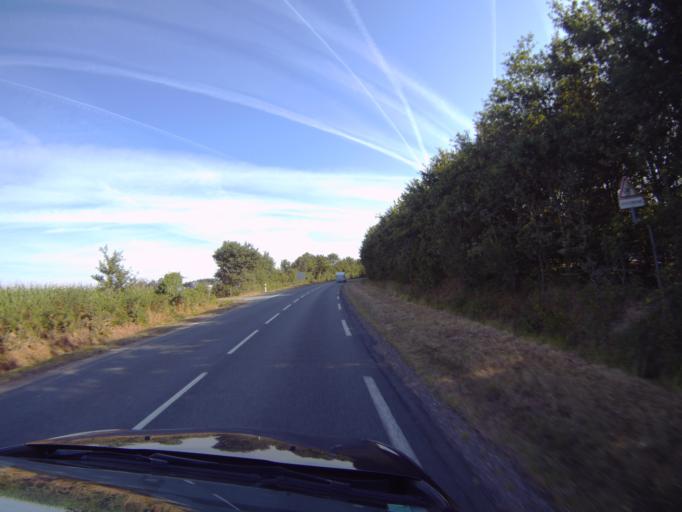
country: FR
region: Pays de la Loire
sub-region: Departement de la Vendee
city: Saint-Hilaire-de-Talmont
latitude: 46.4927
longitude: -1.5843
